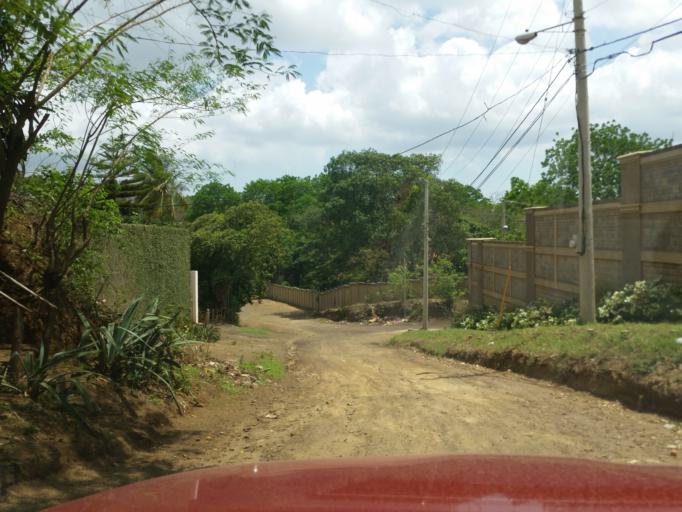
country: NI
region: Managua
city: Managua
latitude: 12.0733
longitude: -86.2420
